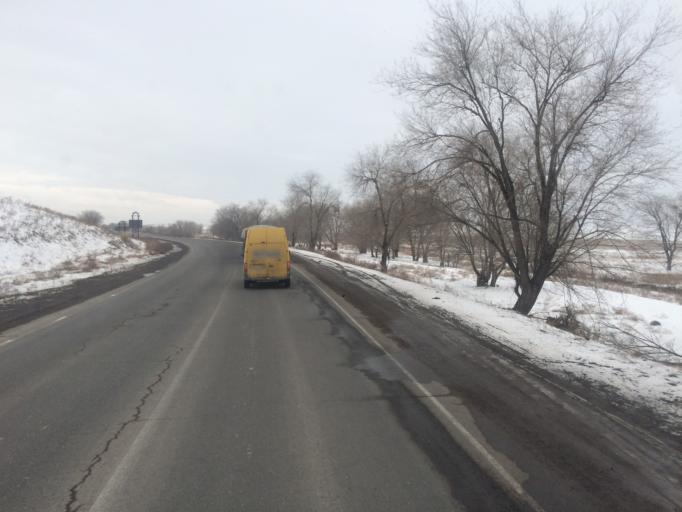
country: KG
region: Chuy
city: Bystrovka
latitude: 43.3300
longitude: 75.8300
